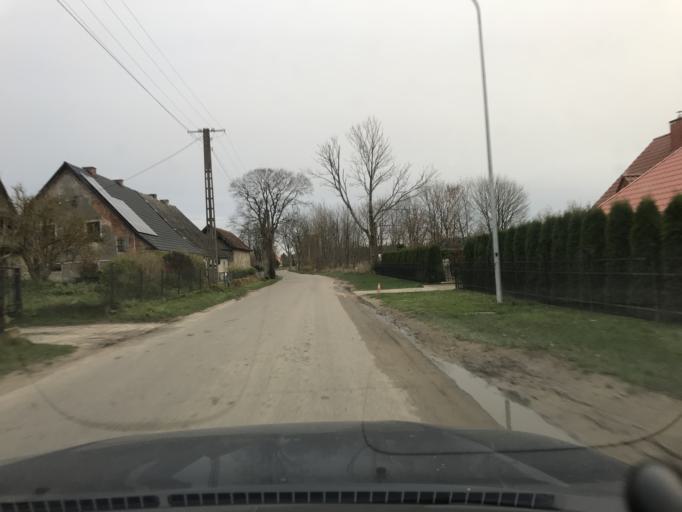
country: PL
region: Pomeranian Voivodeship
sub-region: Powiat slupski
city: Kobylnica
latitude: 54.4457
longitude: 16.8877
